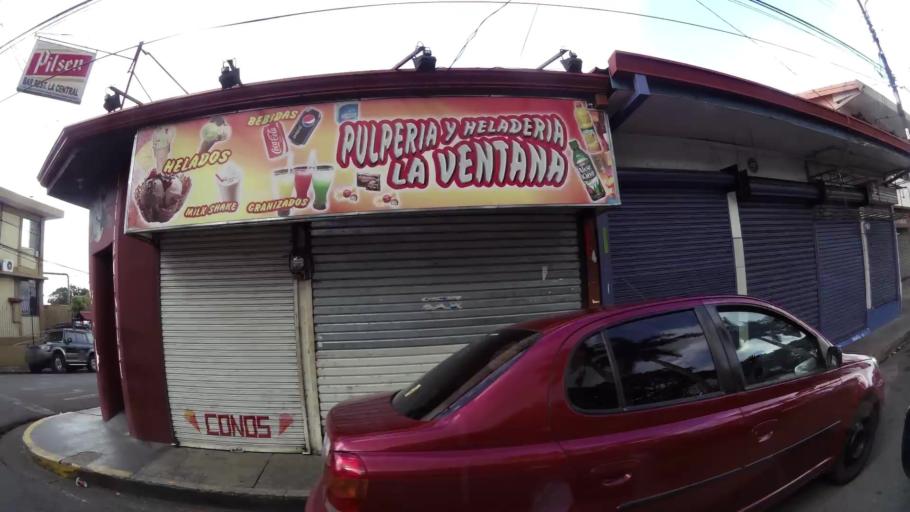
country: CR
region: San Jose
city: Escazu
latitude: 9.9204
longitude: -84.1398
